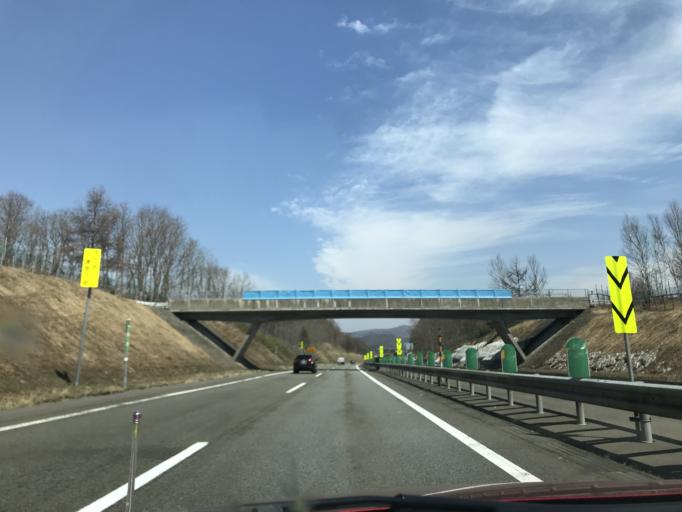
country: JP
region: Hokkaido
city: Iwamizawa
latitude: 43.2106
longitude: 141.8183
